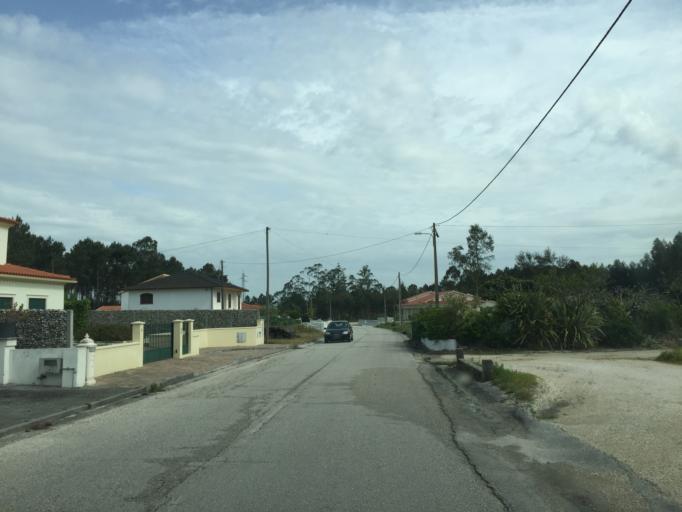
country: PT
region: Coimbra
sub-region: Figueira da Foz
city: Lavos
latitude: 40.0170
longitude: -8.8229
